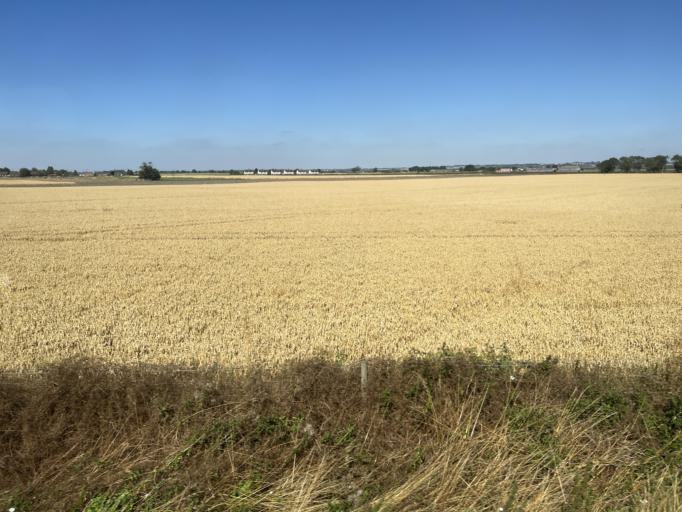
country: GB
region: England
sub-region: Lincolnshire
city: Spilsby
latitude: 53.0952
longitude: 0.1039
